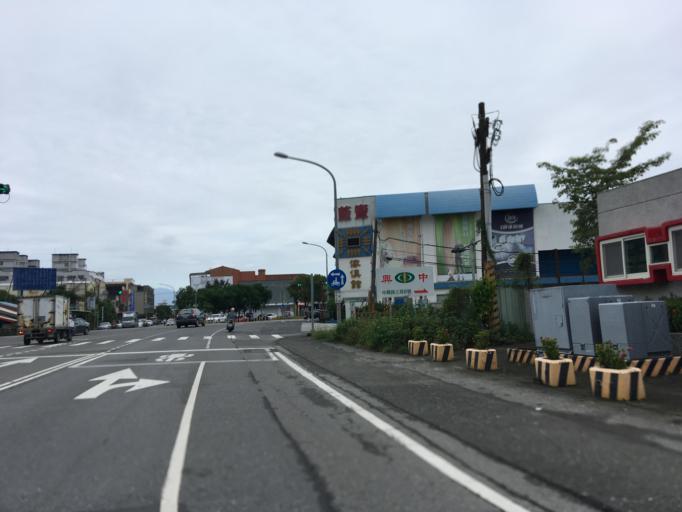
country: TW
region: Taiwan
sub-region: Yilan
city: Yilan
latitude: 24.6984
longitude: 121.7690
